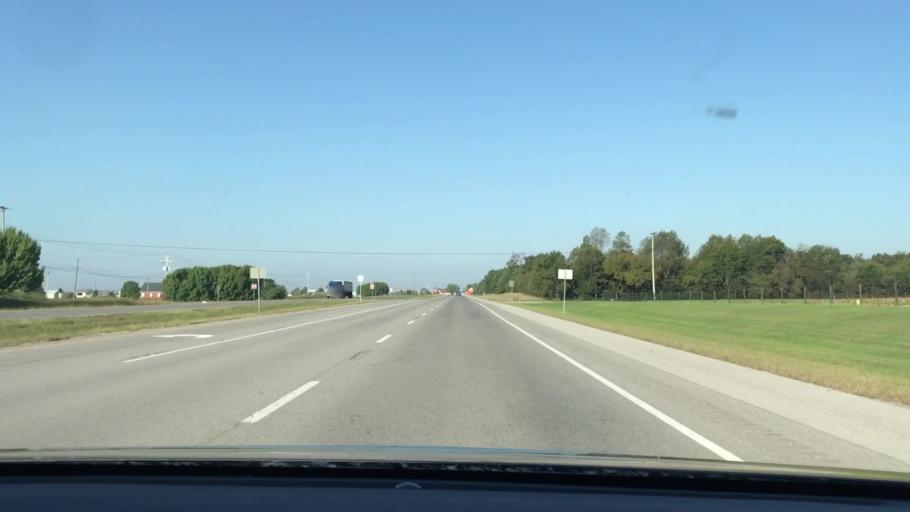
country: US
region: Kentucky
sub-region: Trigg County
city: Cadiz
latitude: 36.8678
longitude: -87.7821
